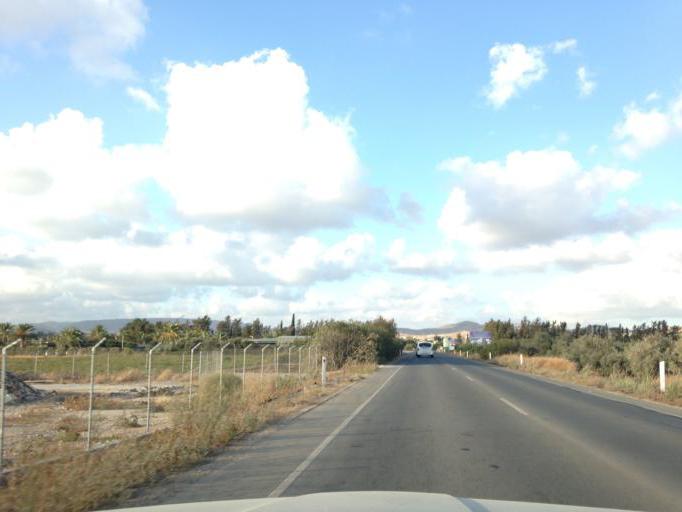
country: CY
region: Pafos
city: Paphos
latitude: 34.7224
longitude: 32.5148
